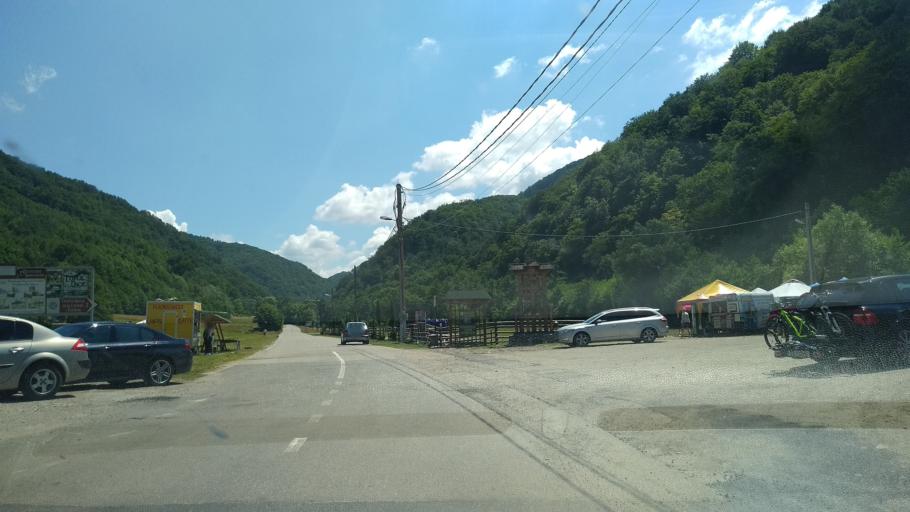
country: RO
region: Hunedoara
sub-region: Comuna Orastioara de Sus
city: Orastioara de Sus
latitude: 45.6801
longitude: 23.1619
